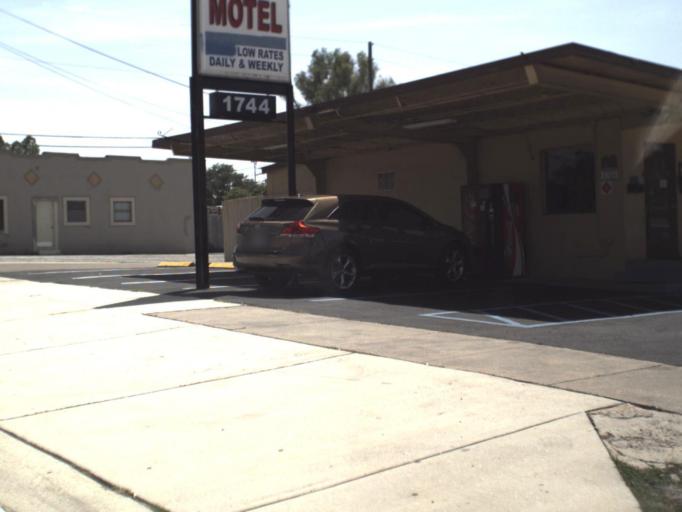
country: US
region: Florida
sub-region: Pinellas County
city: Clearwater
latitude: 27.9845
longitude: -82.7960
